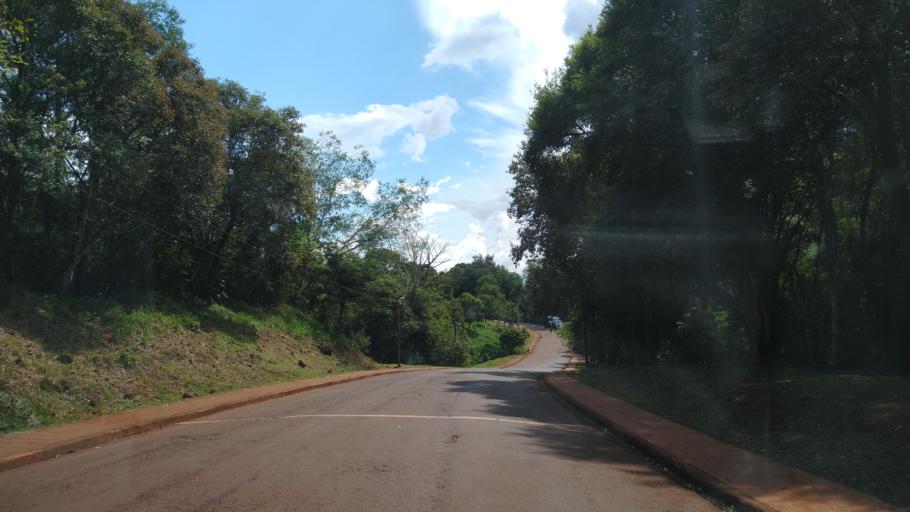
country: AR
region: Misiones
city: Puerto Libertad
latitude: -25.9688
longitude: -54.5818
